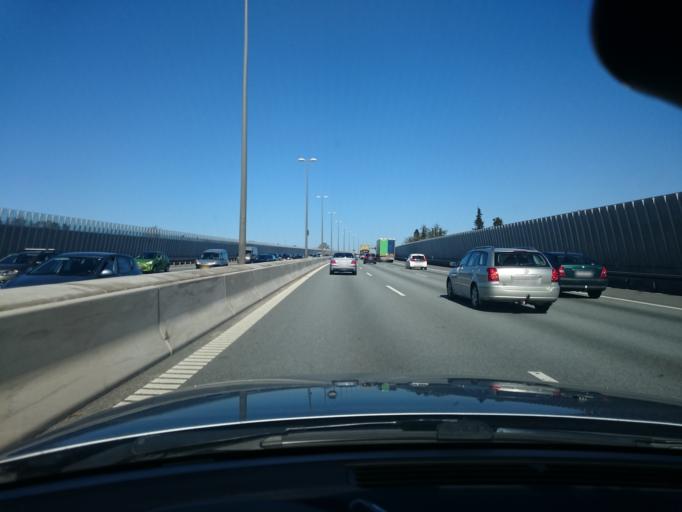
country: DK
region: Capital Region
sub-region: Gladsaxe Municipality
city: Buddinge
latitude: 55.7478
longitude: 12.4672
